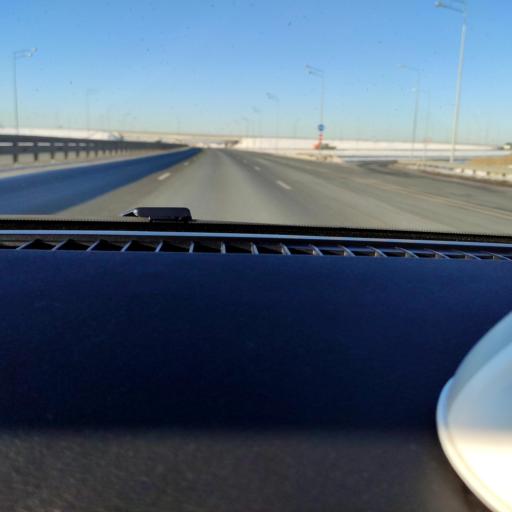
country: RU
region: Samara
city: Smyshlyayevka
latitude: 53.1479
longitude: 50.3985
